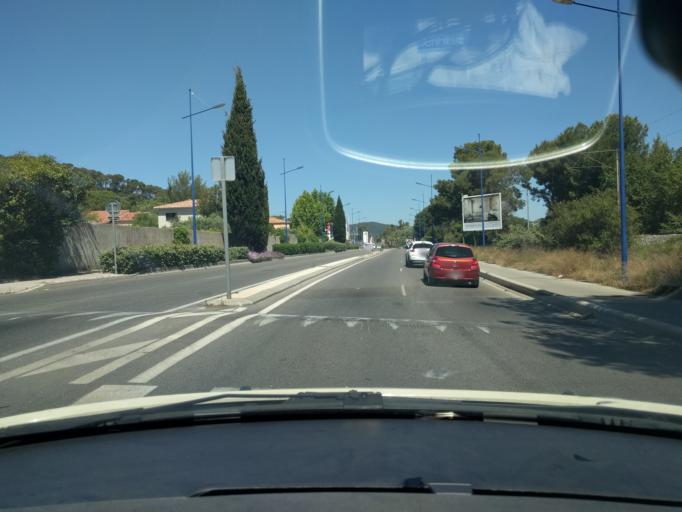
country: FR
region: Provence-Alpes-Cote d'Azur
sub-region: Departement du Var
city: Hyeres
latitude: 43.1025
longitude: 6.1293
